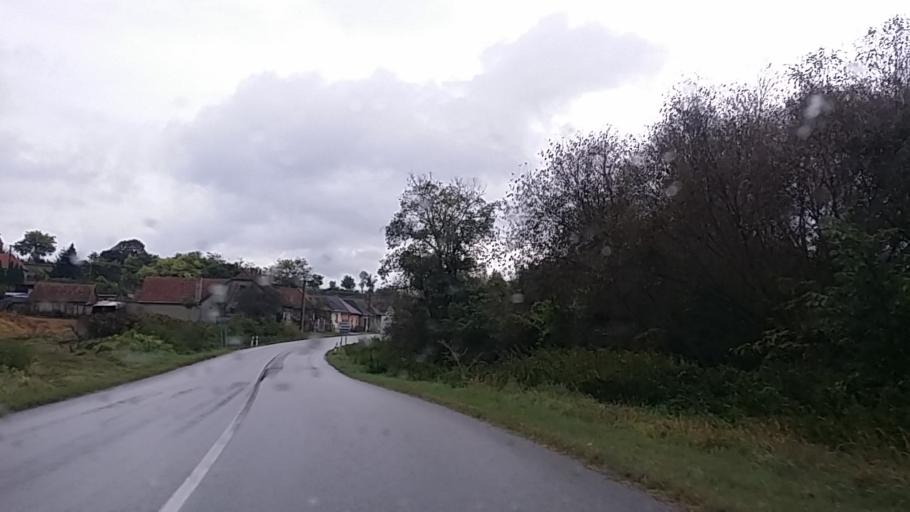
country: SK
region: Nitriansky
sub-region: Okres Nove Zamky
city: Sturovo
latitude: 47.8354
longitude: 18.7230
